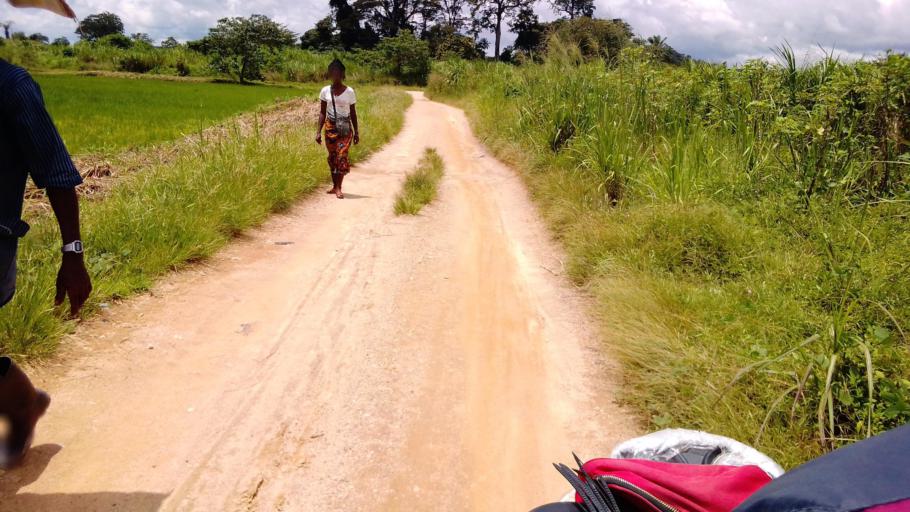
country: SL
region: Eastern Province
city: Koidu
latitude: 8.6747
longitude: -10.9578
